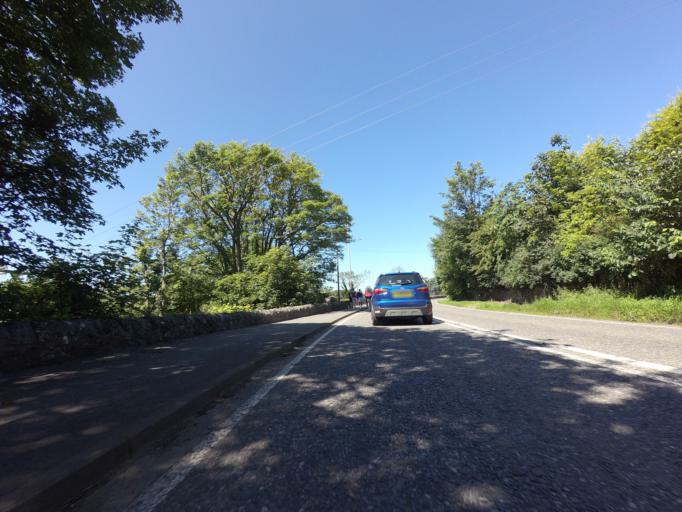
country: GB
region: Scotland
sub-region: Aberdeenshire
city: Macduff
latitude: 57.6594
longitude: -2.5113
